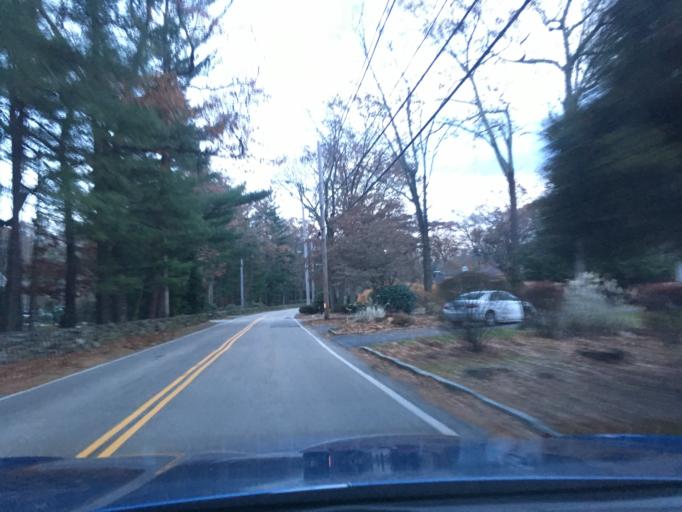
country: US
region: Rhode Island
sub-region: Kent County
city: East Greenwich
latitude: 41.6777
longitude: -71.4588
